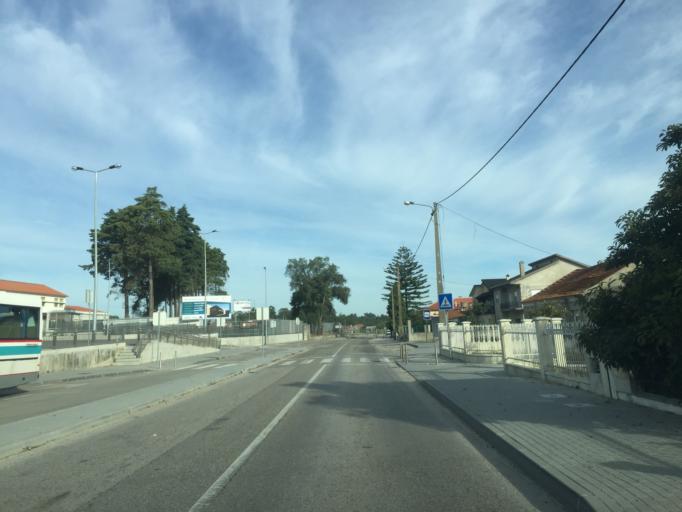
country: PT
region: Leiria
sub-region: Leiria
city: Monte Redondo
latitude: 39.9518
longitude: -8.7856
